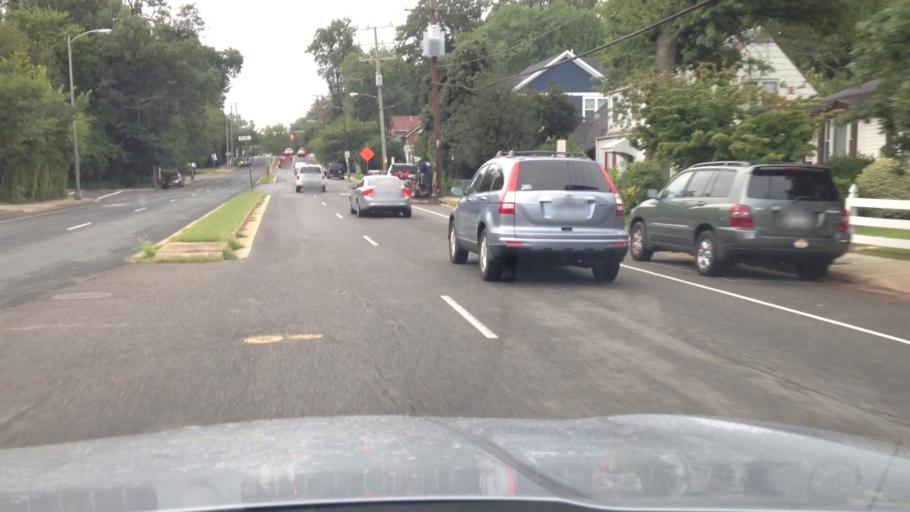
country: US
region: Virginia
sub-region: Fairfax County
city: Seven Corners
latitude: 38.8805
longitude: -77.1544
